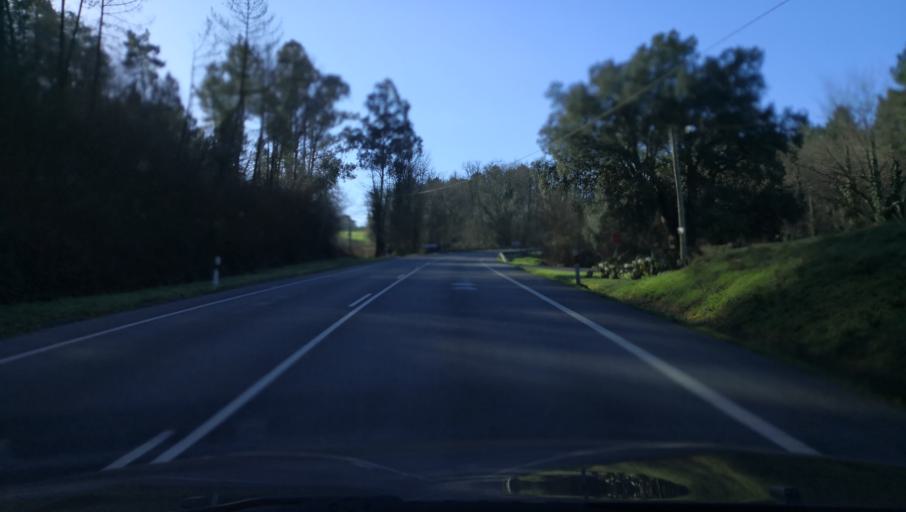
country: ES
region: Galicia
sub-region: Provincia da Coruna
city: Ribeira
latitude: 42.7674
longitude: -8.3982
